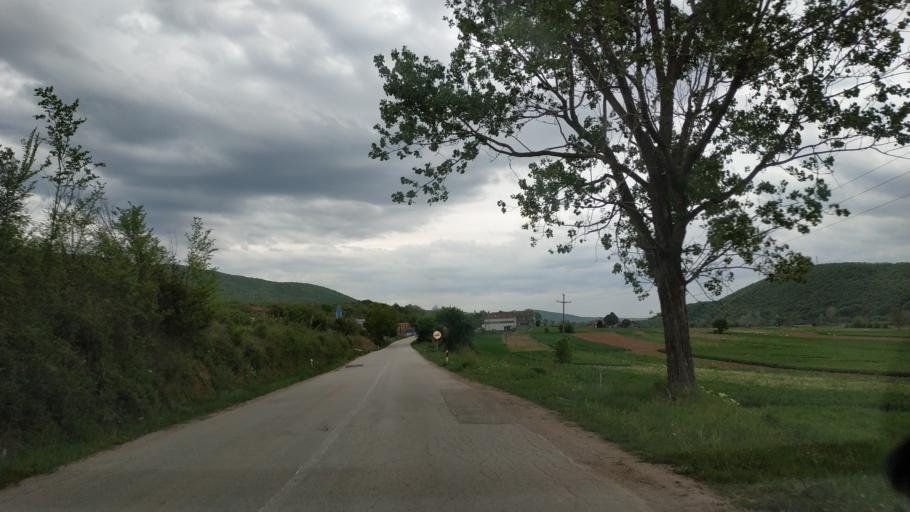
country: RS
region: Central Serbia
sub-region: Nisavski Okrug
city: Aleksinac
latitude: 43.5988
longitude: 21.6876
